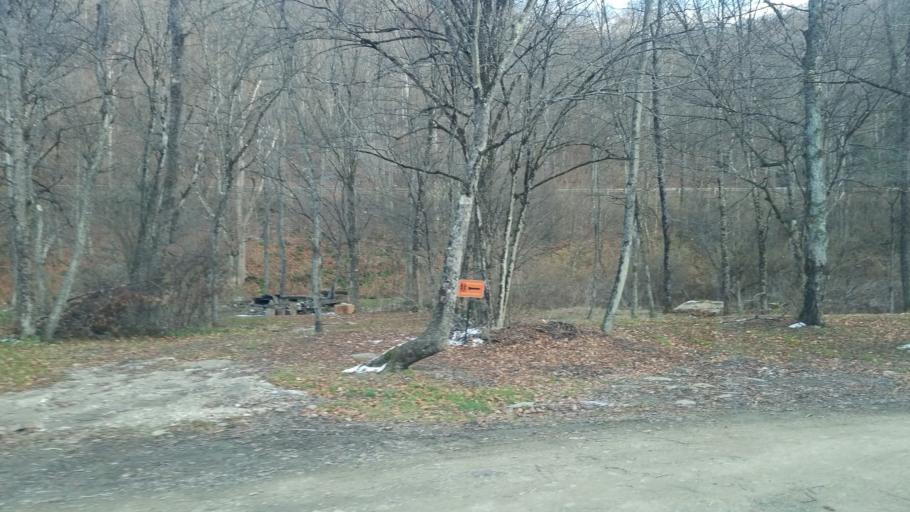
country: US
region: Pennsylvania
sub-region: Potter County
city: Coudersport
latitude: 41.6519
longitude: -78.0861
